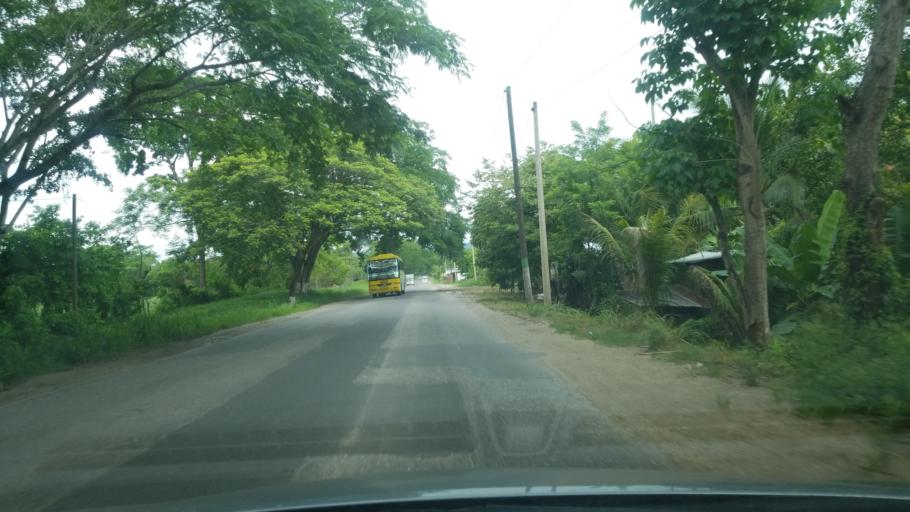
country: HN
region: Santa Barbara
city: La Flecha
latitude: 15.2962
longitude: -88.4612
